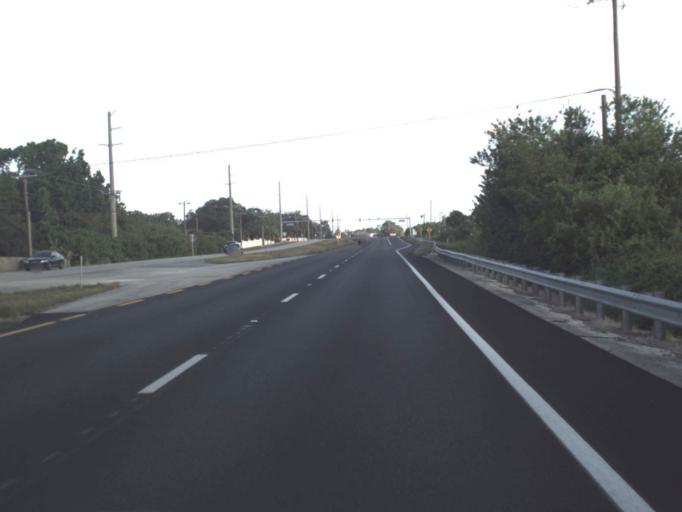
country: US
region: Florida
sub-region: Brevard County
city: Rockledge
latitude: 28.2646
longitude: -80.6893
